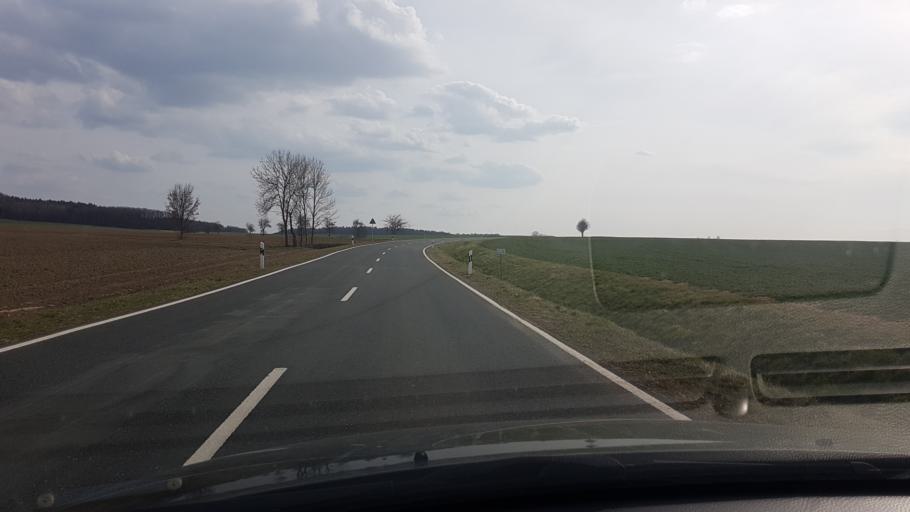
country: DE
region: Bavaria
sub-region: Upper Franconia
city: Schesslitz
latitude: 50.0306
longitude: 11.0077
